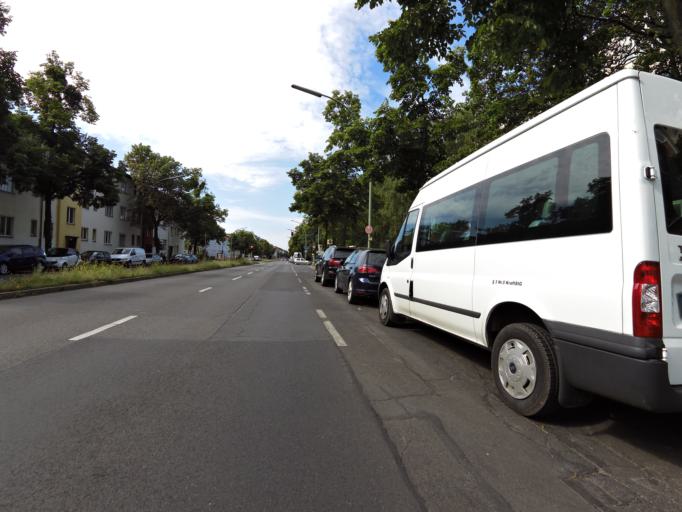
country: DE
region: Berlin
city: Lankwitz
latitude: 52.4385
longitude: 13.3491
